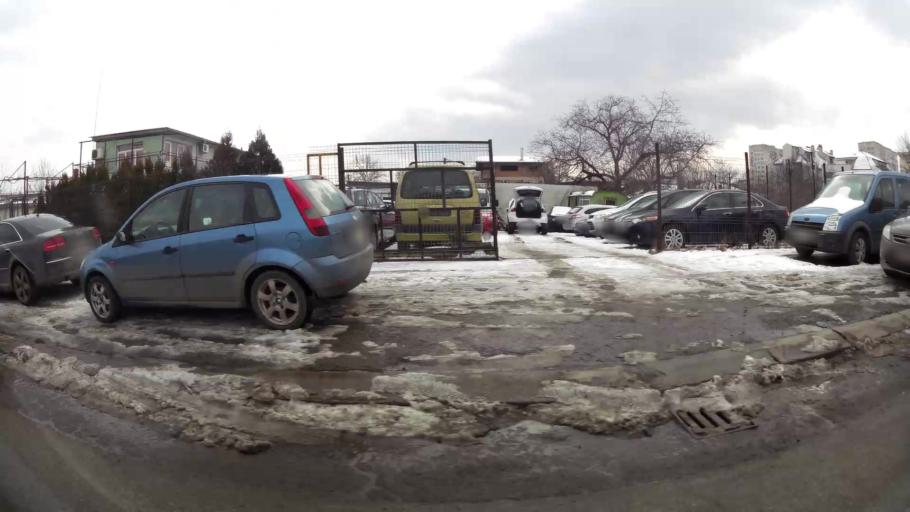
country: BG
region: Sofia-Capital
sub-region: Stolichna Obshtina
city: Sofia
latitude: 42.7085
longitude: 23.3721
